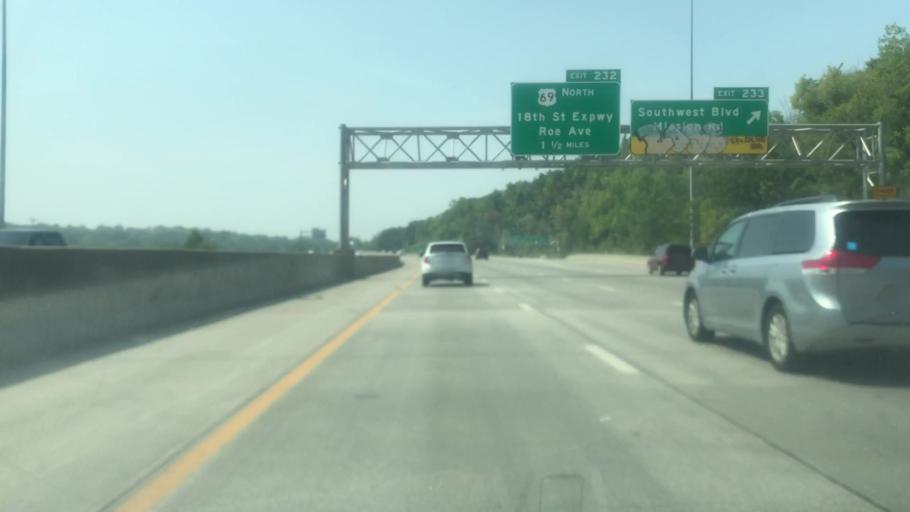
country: US
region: Kansas
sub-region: Johnson County
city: Westwood
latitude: 39.0650
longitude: -94.6231
